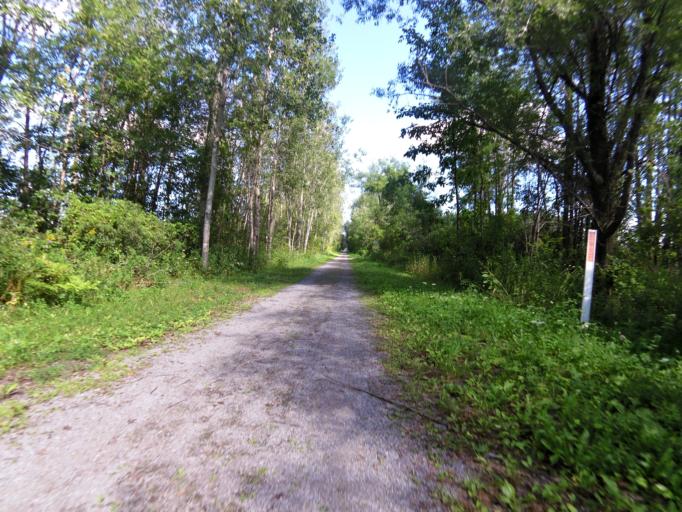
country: CA
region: Ontario
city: Ottawa
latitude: 45.1712
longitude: -75.6172
